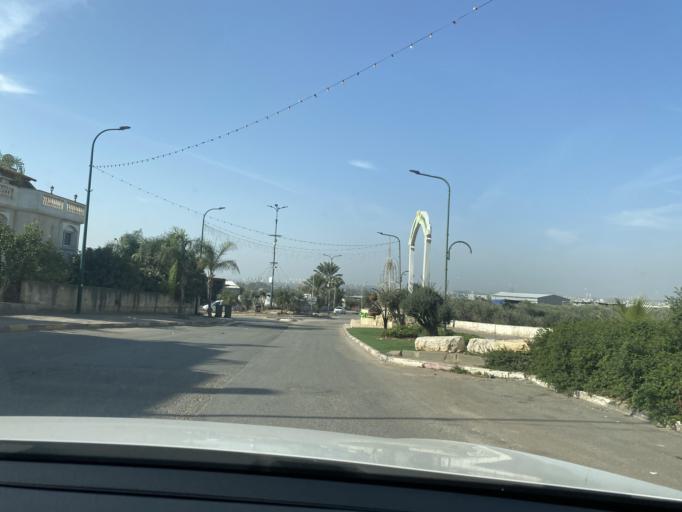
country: IL
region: Central District
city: Kafr Qasim
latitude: 32.1319
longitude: 34.9656
